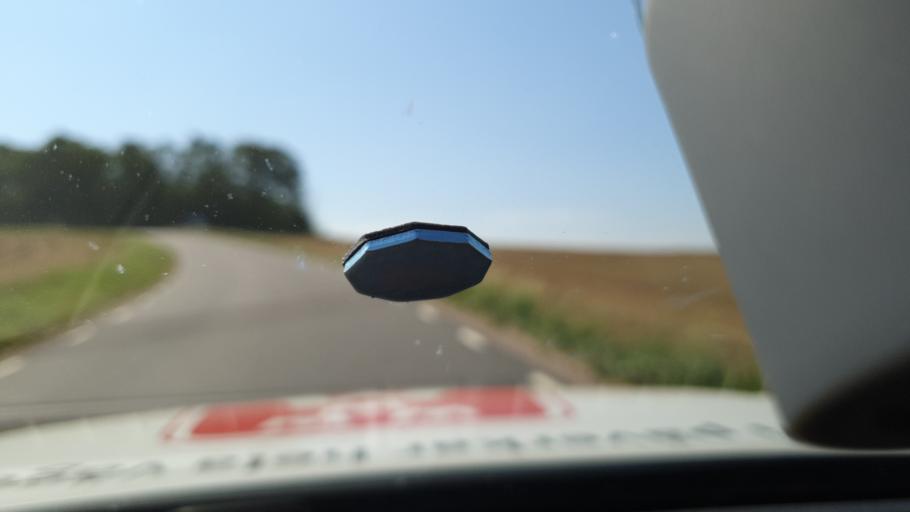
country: SE
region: Skane
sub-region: Sjobo Kommun
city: Blentarp
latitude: 55.5600
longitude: 13.5629
